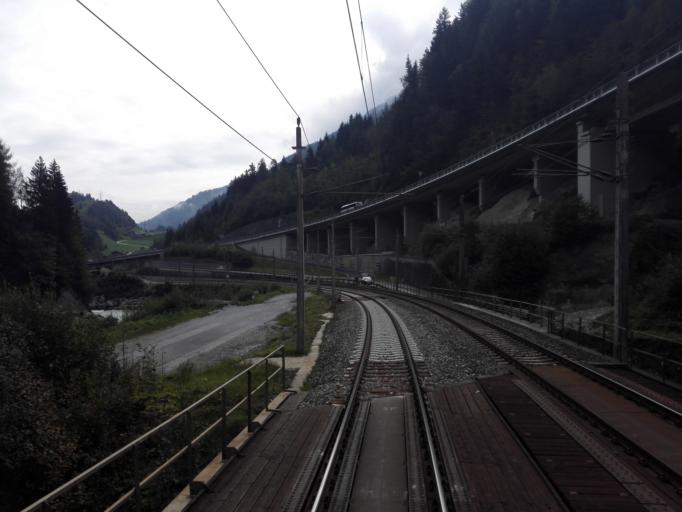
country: AT
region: Salzburg
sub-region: Politischer Bezirk Sankt Johann im Pongau
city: Goldegg
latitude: 47.3014
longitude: 13.1010
